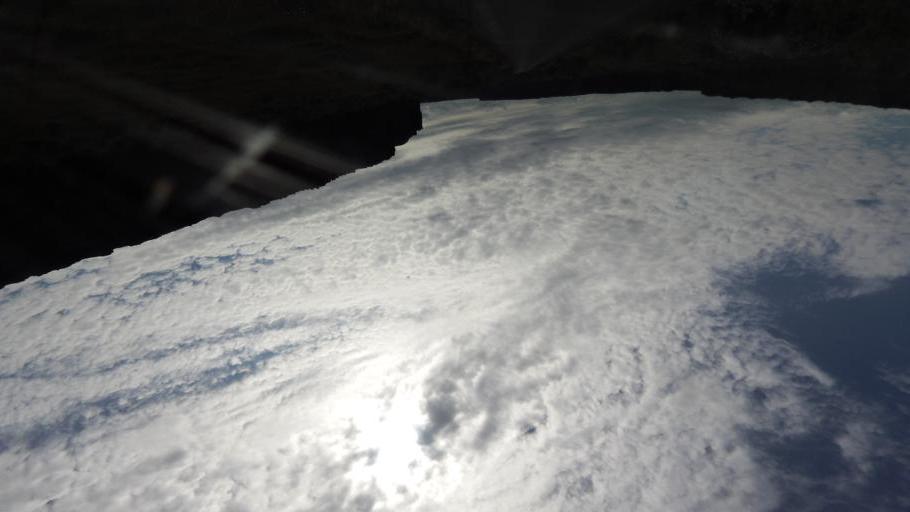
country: IS
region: Northeast
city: Husavik
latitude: 66.0193
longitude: -16.4967
